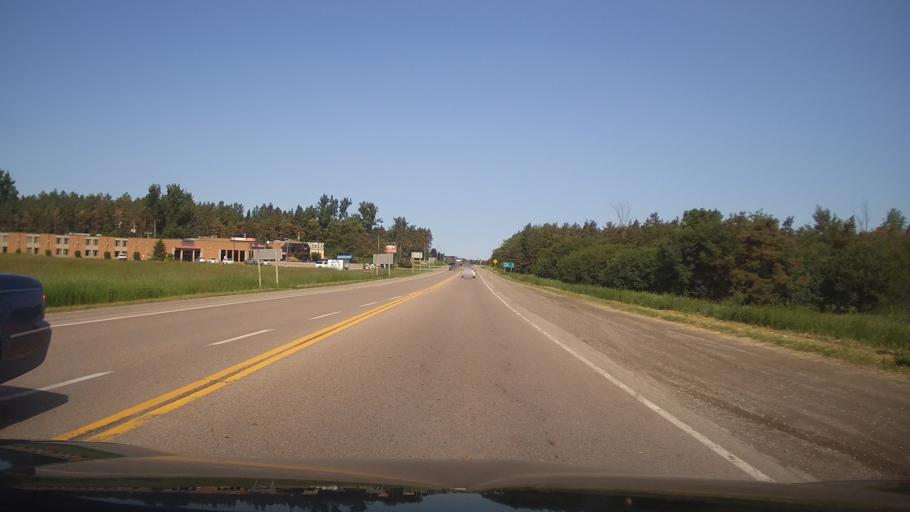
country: CA
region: Ontario
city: Omemee
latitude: 44.3466
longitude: -78.7771
